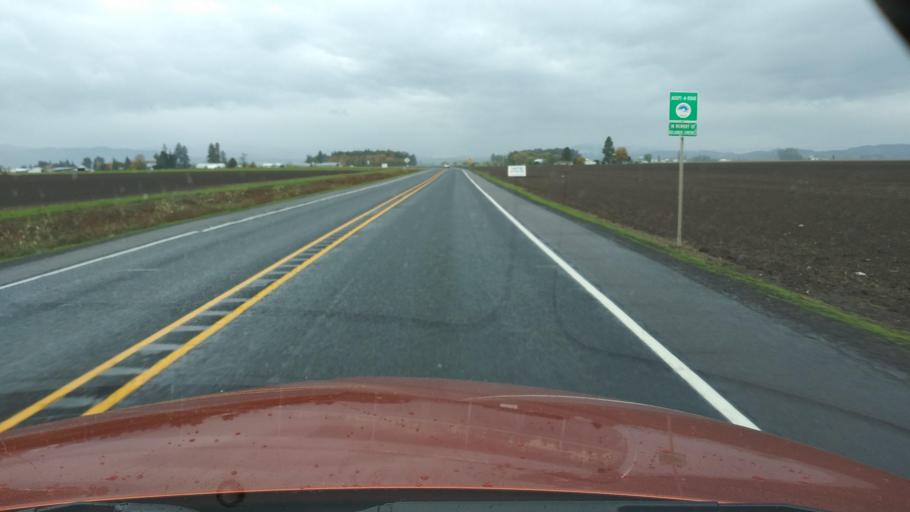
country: US
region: Oregon
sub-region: Washington County
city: North Plains
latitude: 45.5737
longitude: -123.0209
